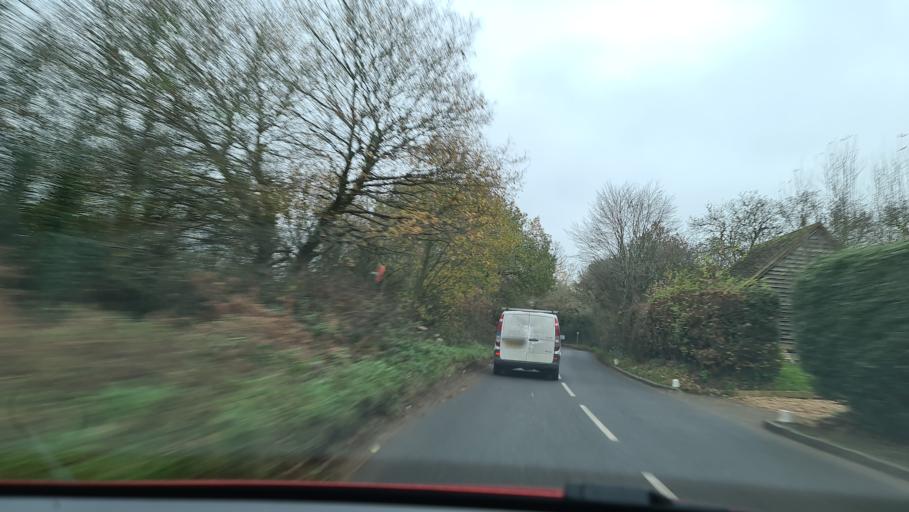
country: GB
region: England
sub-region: Buckinghamshire
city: Seer Green
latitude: 51.6226
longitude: -0.5904
